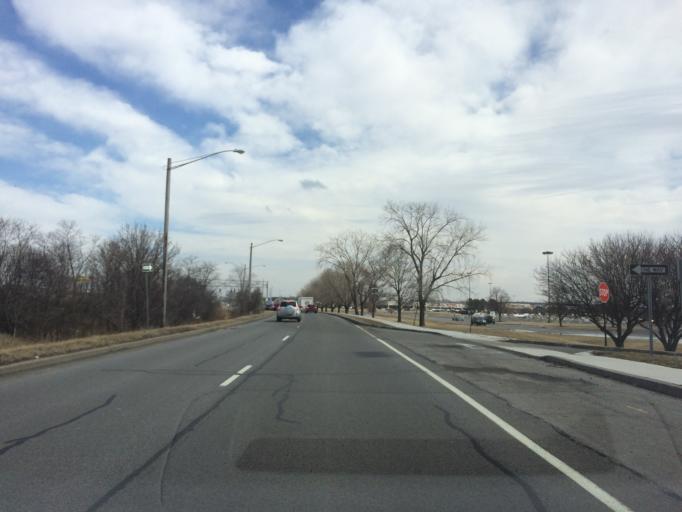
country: US
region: New York
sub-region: Monroe County
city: Rochester
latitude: 43.0873
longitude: -77.6345
